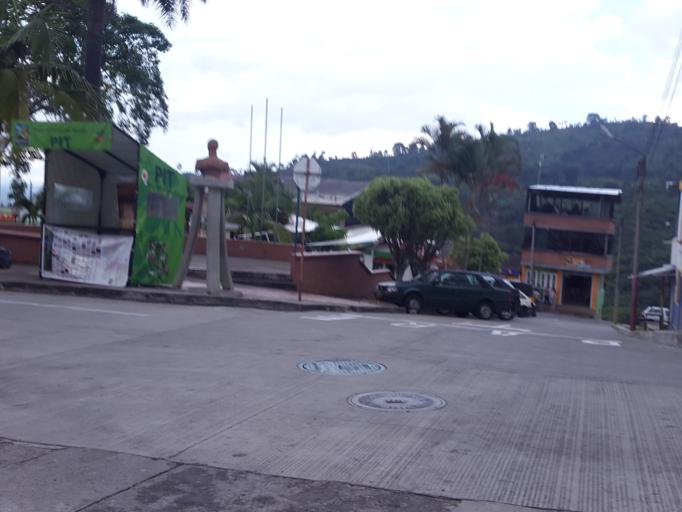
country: CO
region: Quindio
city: Buenavista
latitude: 4.3590
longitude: -75.7383
